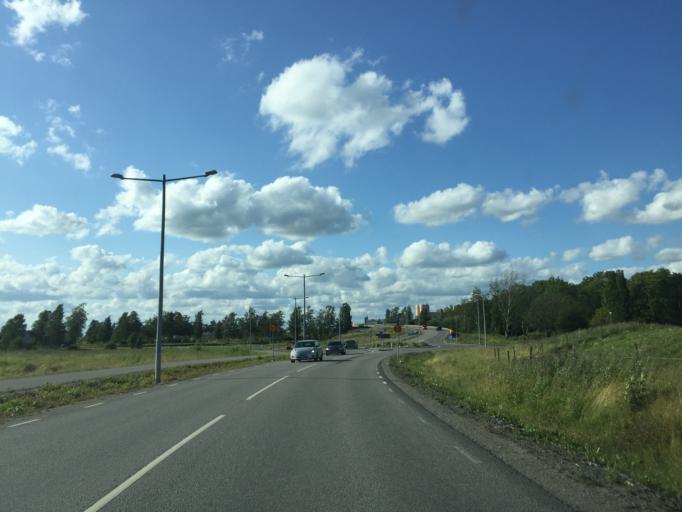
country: SE
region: OErebro
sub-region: Orebro Kommun
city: Orebro
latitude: 59.2523
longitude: 15.1871
